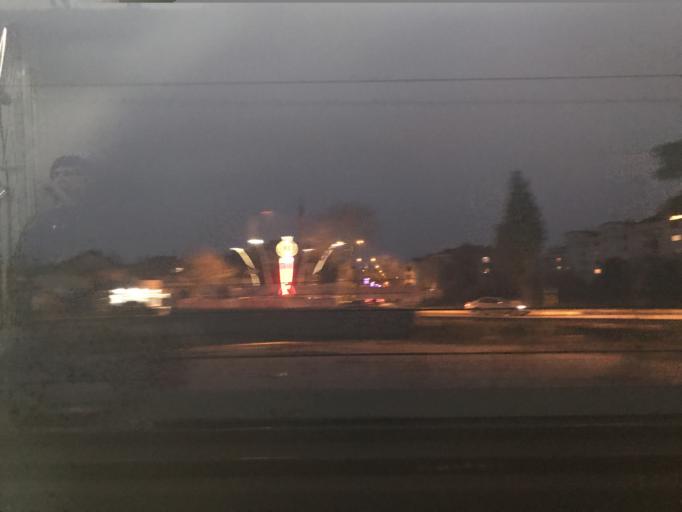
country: TR
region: Istanbul
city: Icmeler
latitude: 40.8269
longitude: 29.3263
